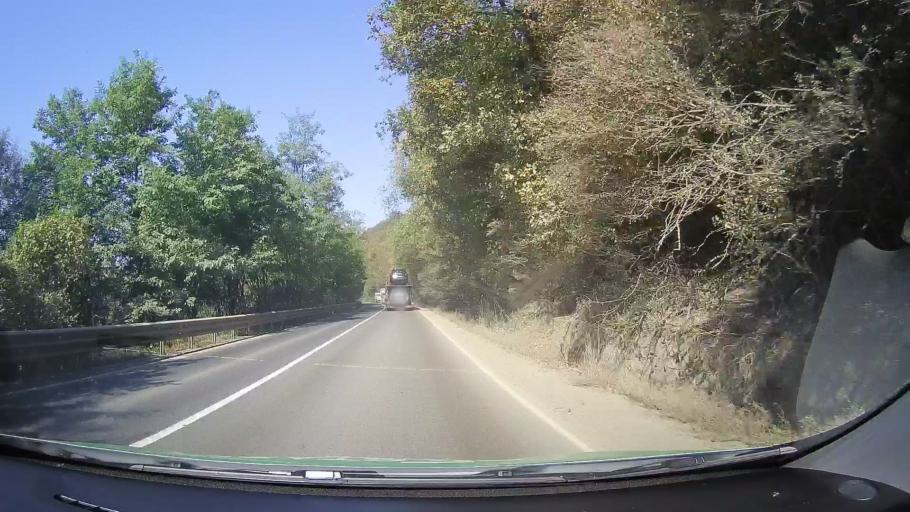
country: RO
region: Arad
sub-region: Comuna Bata
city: Bata
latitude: 46.0657
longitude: 22.0431
